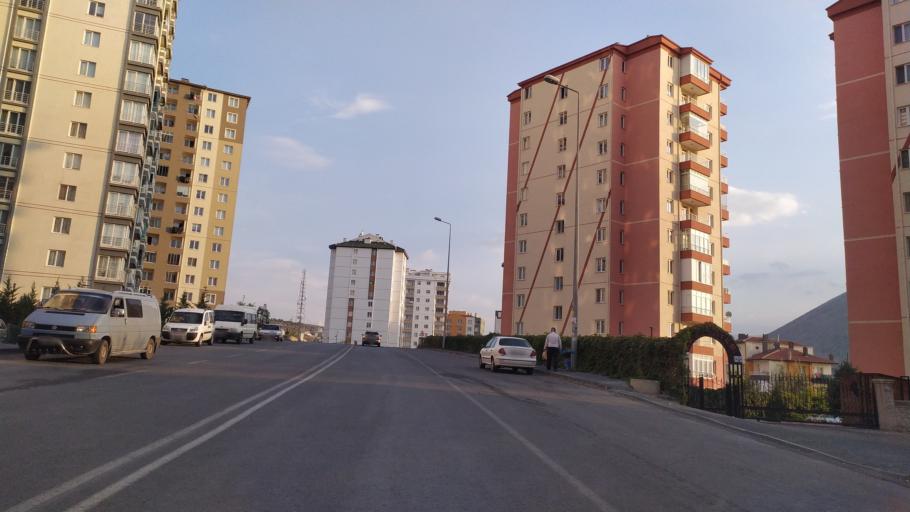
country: TR
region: Kayseri
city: Talas
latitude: 38.7009
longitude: 35.5637
